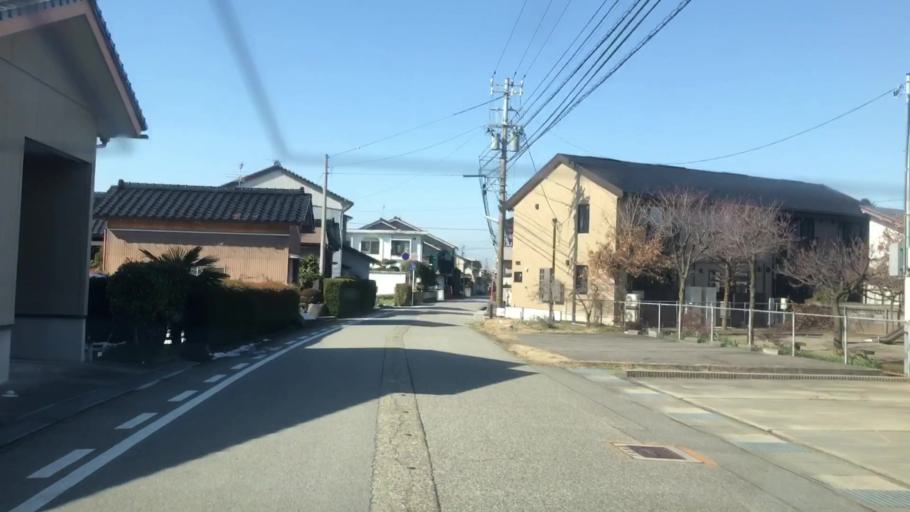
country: JP
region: Toyama
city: Toyama-shi
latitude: 36.6796
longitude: 137.2393
